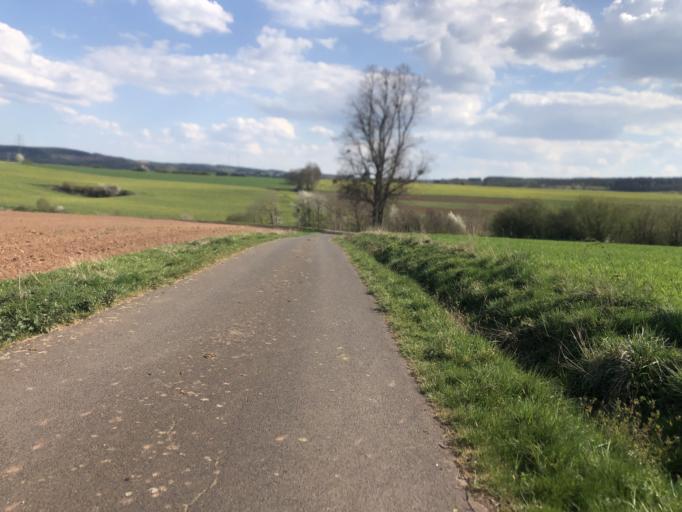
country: DE
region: North Rhine-Westphalia
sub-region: Regierungsbezirk Koln
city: Kall
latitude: 50.5962
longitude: 6.5555
